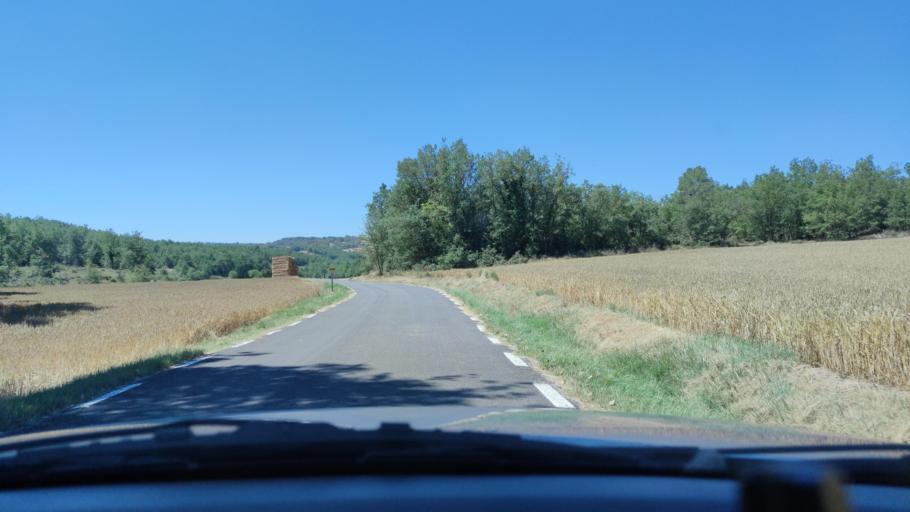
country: ES
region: Catalonia
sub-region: Provincia de Lleida
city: Tora de Riubregos
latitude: 41.9040
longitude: 1.4451
